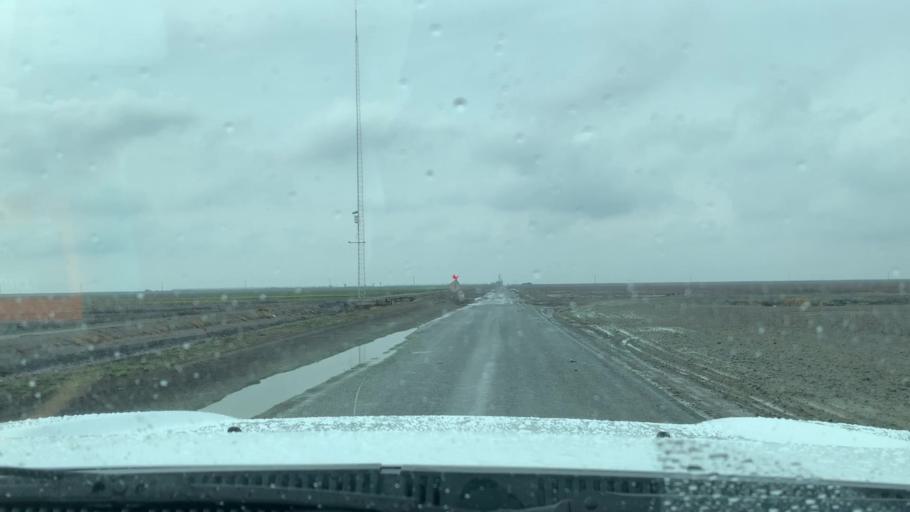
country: US
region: California
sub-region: Kings County
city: Corcoran
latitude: 36.0072
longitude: -119.5259
